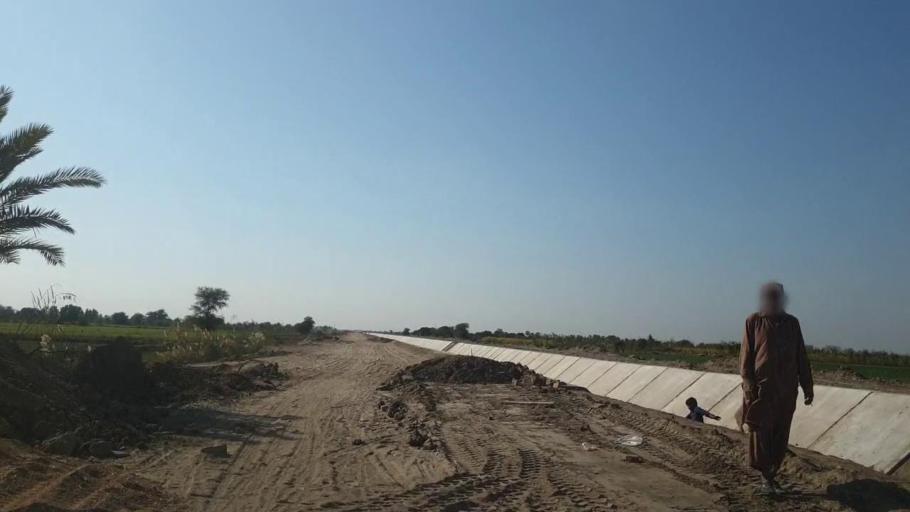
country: PK
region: Sindh
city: Mirpur Khas
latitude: 25.6450
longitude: 69.0559
